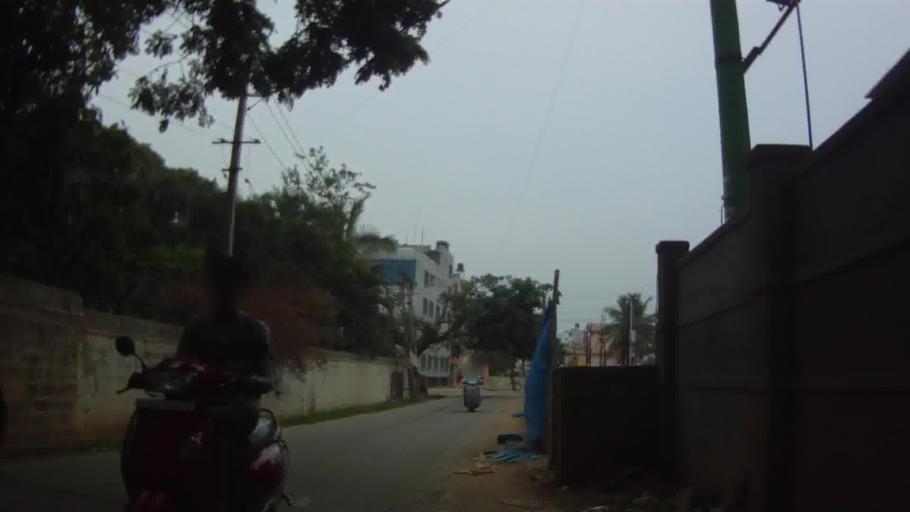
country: IN
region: Karnataka
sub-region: Bangalore Urban
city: Bangalore
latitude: 12.9564
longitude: 77.7219
